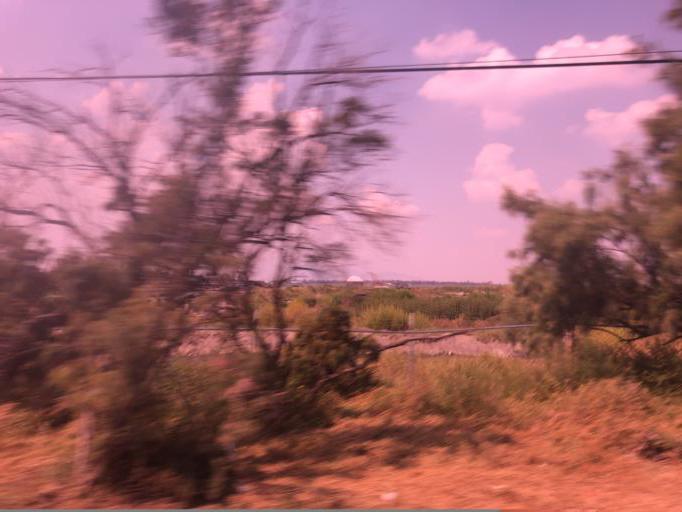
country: MX
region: Mexico
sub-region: Ciudad Nezahualcoyotl
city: Colonia Gustavo Baz Prada
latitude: 19.4634
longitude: -99.0215
